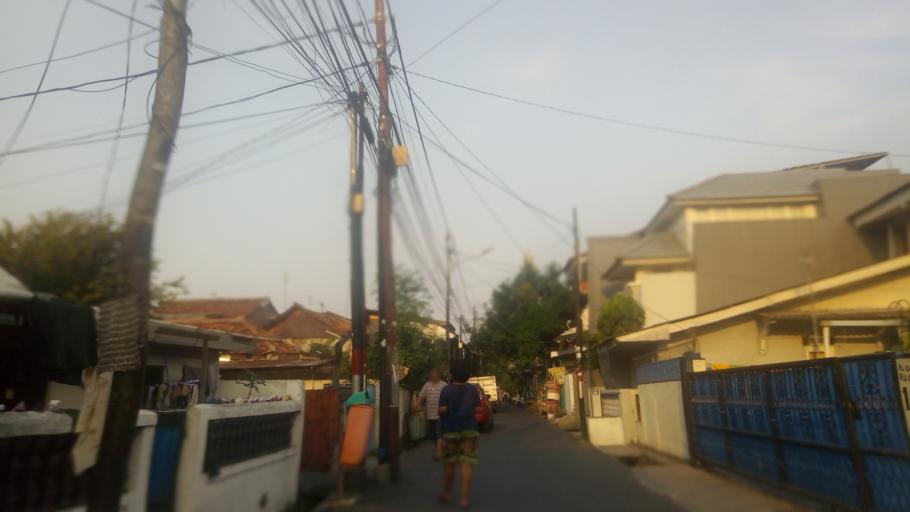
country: ID
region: Jakarta Raya
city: Jakarta
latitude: -6.2050
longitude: 106.8523
